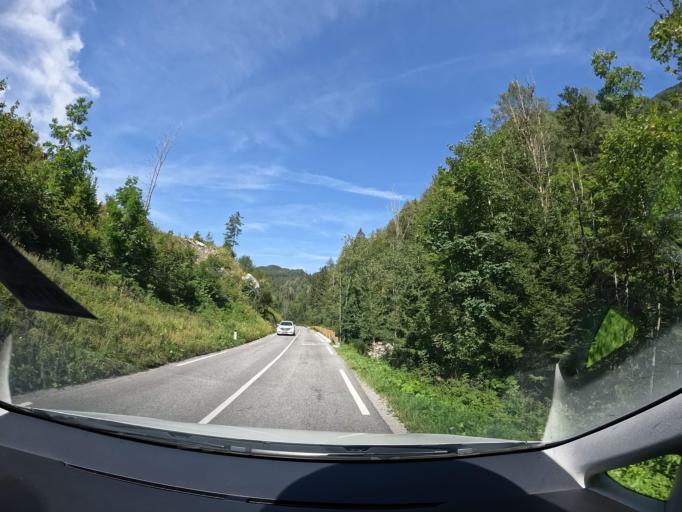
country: SI
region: Zirovnica
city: Zirovnica
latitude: 46.4249
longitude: 14.1295
